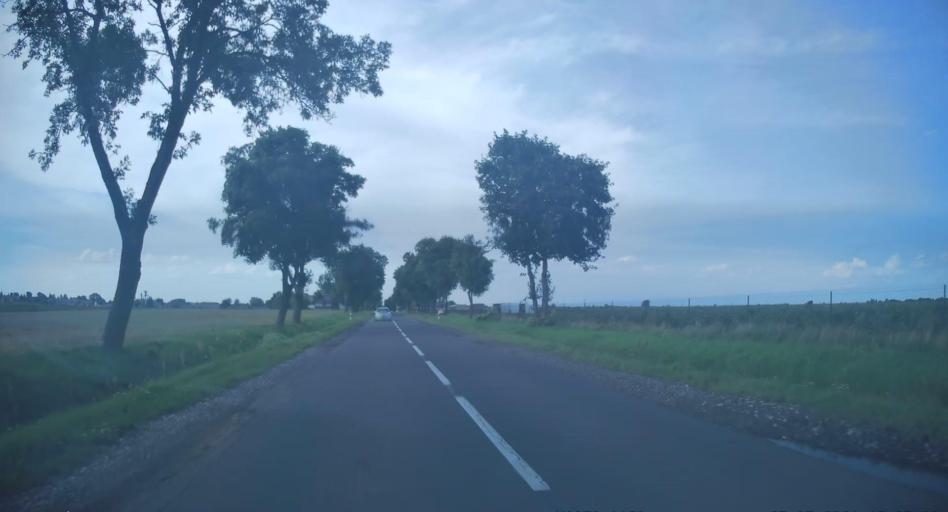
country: PL
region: Lodz Voivodeship
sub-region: Powiat tomaszowski
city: Rzeczyca
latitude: 51.6233
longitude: 20.2928
